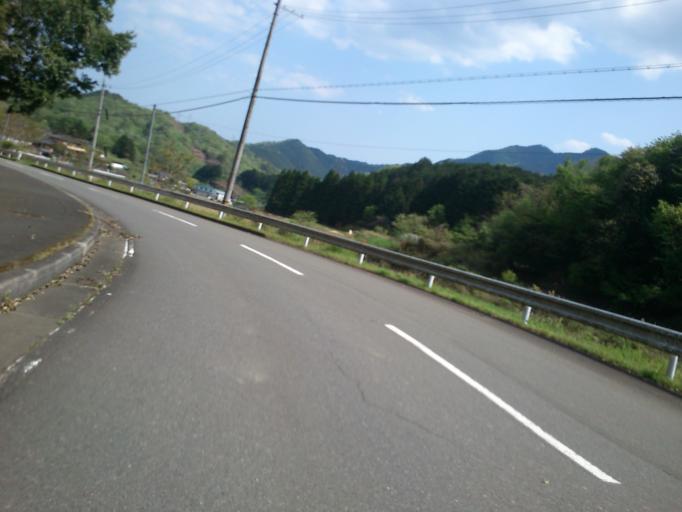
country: JP
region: Kyoto
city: Fukuchiyama
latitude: 35.3310
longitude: 134.9323
